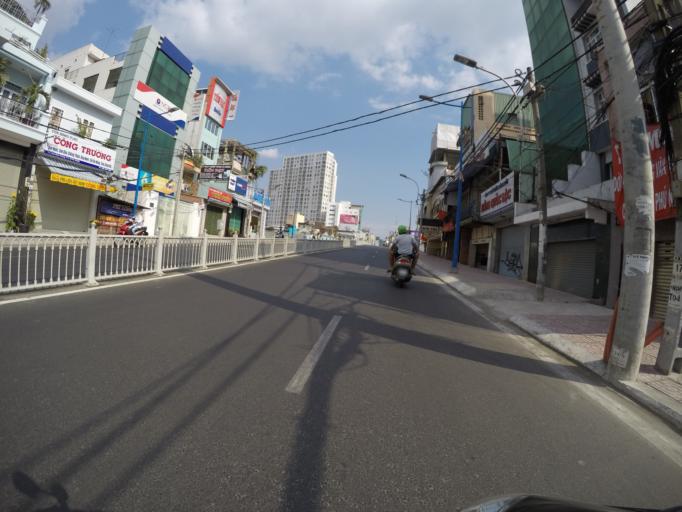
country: VN
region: Ho Chi Minh City
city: Quan Phu Nhuan
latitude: 10.7927
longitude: 106.6857
